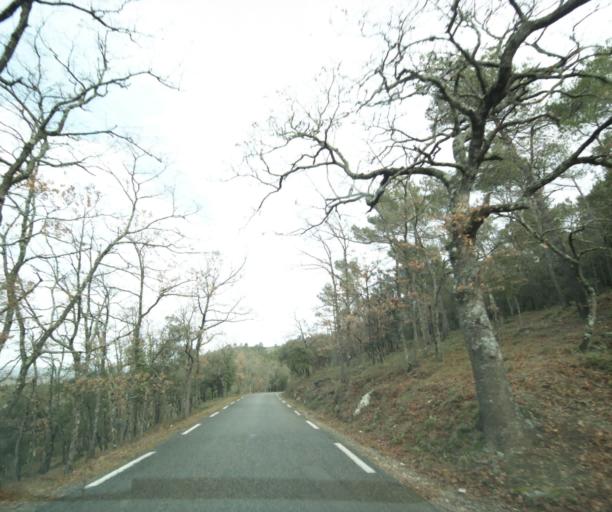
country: FR
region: Provence-Alpes-Cote d'Azur
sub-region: Departement du Var
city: Tourves
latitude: 43.3806
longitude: 5.8958
